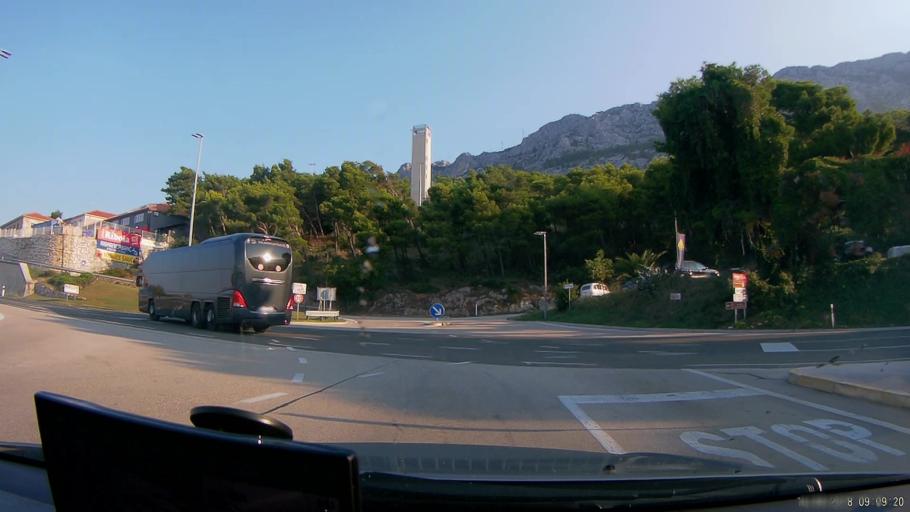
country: HR
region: Splitsko-Dalmatinska
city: Donja Brela
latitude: 43.3748
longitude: 16.9254
